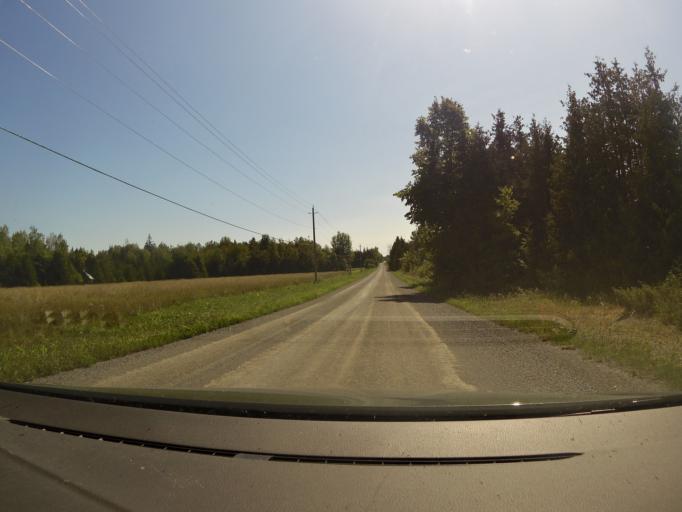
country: CA
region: Ontario
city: Bells Corners
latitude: 45.2678
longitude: -75.9870
